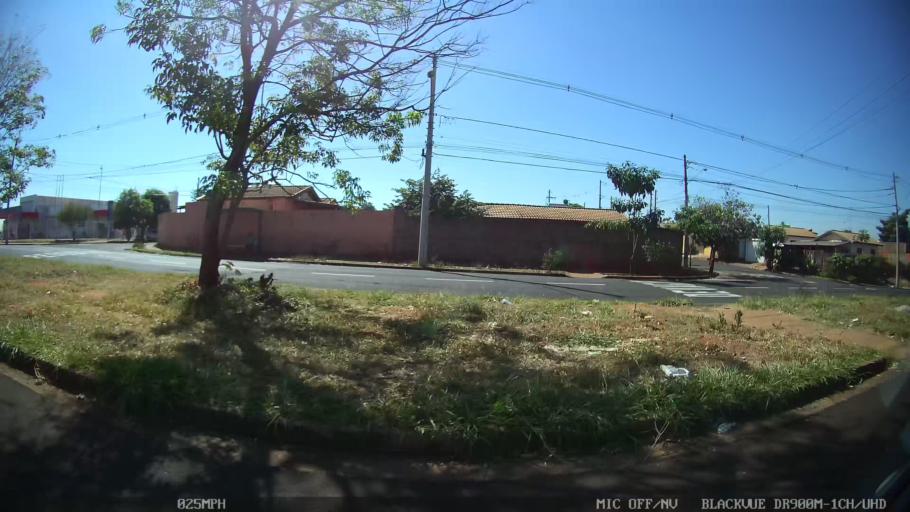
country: BR
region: Sao Paulo
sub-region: Sao Jose Do Rio Preto
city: Sao Jose do Rio Preto
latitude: -20.7418
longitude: -49.4095
